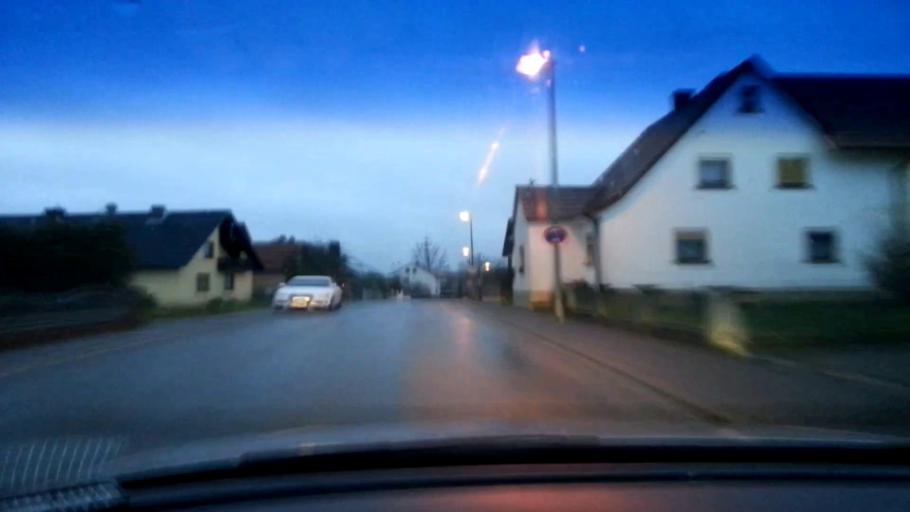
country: DE
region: Bavaria
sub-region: Upper Franconia
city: Memmelsdorf
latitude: 49.9561
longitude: 10.9567
